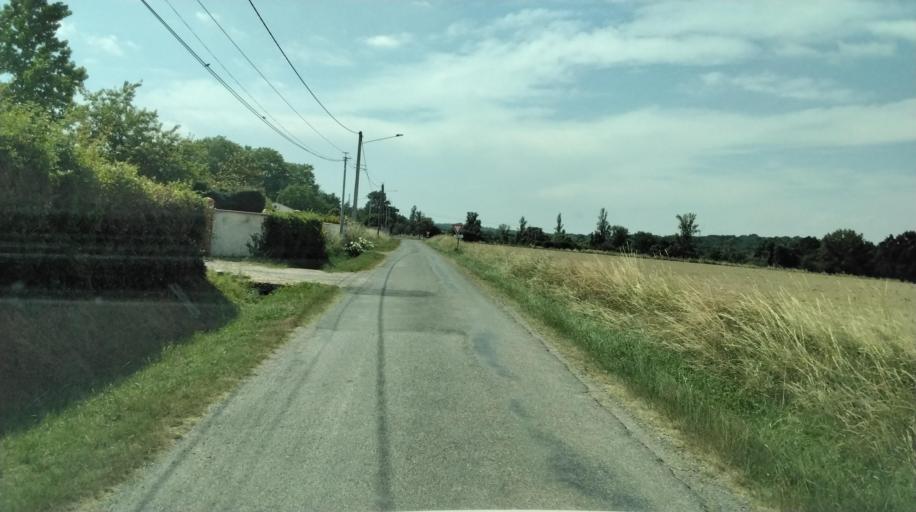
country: FR
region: Midi-Pyrenees
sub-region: Departement de la Haute-Garonne
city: Rieumes
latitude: 43.4156
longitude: 1.1333
